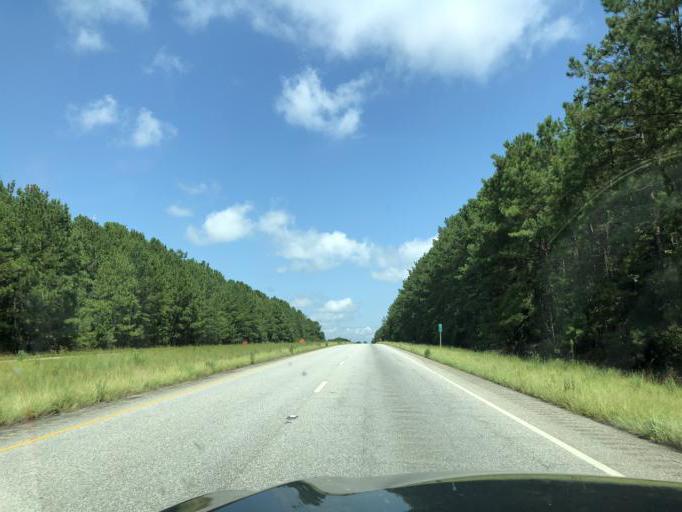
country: US
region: Alabama
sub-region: Henry County
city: Abbeville
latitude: 31.6839
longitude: -85.2790
